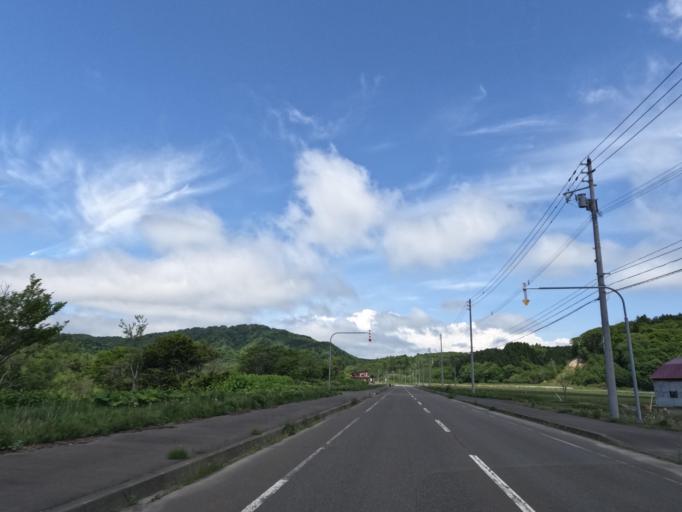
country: JP
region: Hokkaido
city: Tobetsu
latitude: 43.3067
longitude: 141.5544
